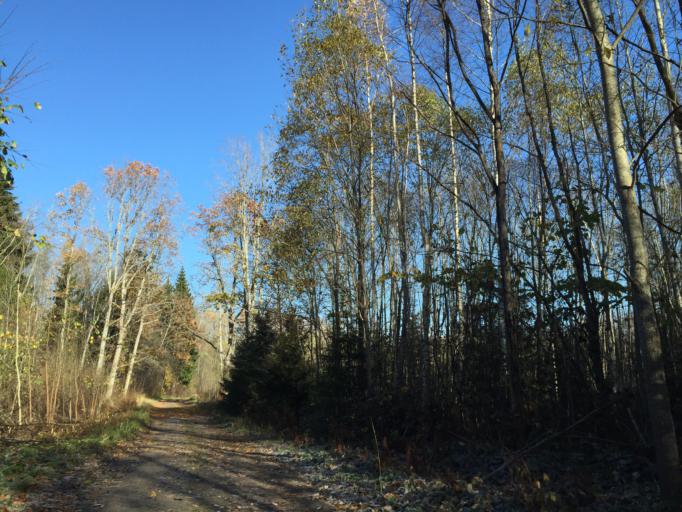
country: LV
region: Aizkraukles Rajons
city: Aizkraukle
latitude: 56.5739
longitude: 25.1779
